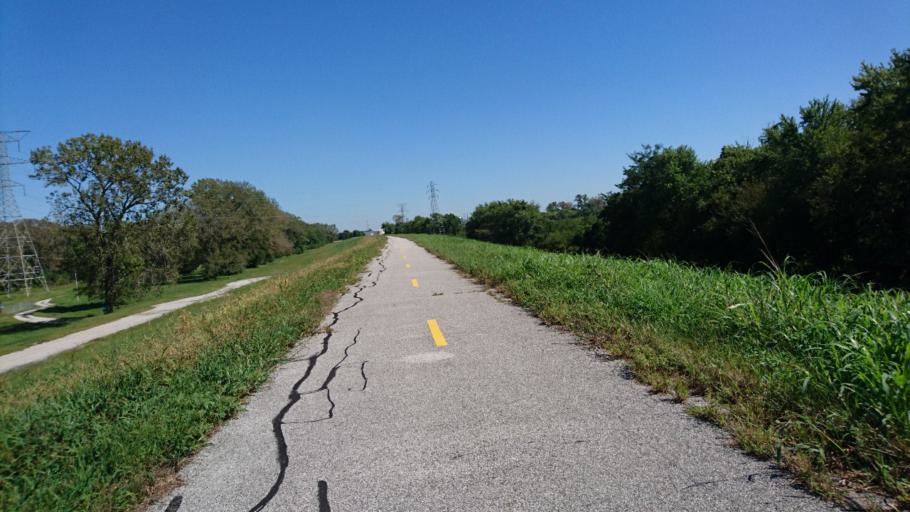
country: US
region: Illinois
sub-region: Madison County
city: Wood River
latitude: 38.8564
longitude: -90.1154
